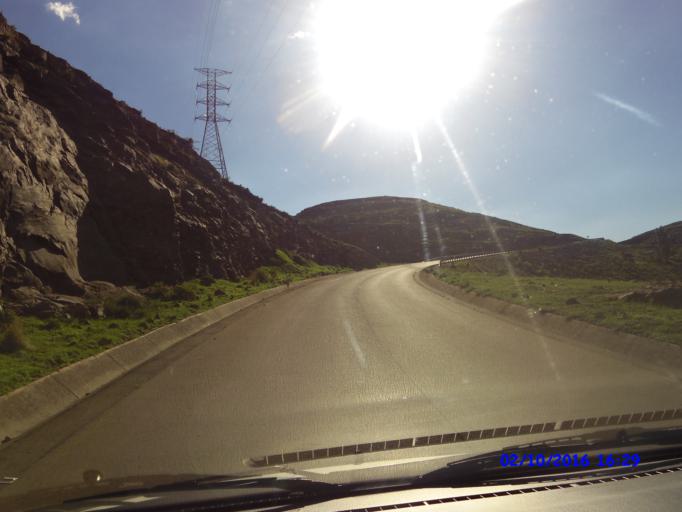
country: LS
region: Maseru
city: Nako
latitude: -29.4752
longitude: 28.0870
